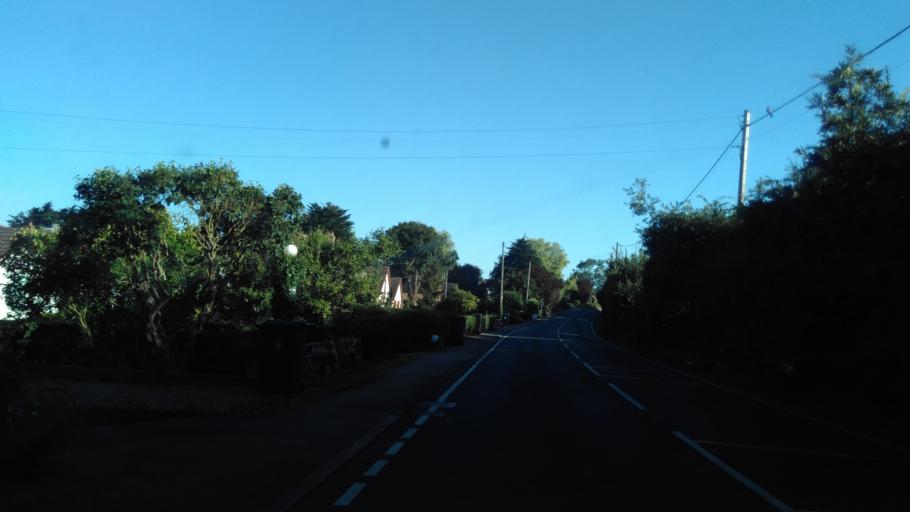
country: GB
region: England
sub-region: Kent
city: Blean
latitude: 51.3279
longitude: 1.0254
